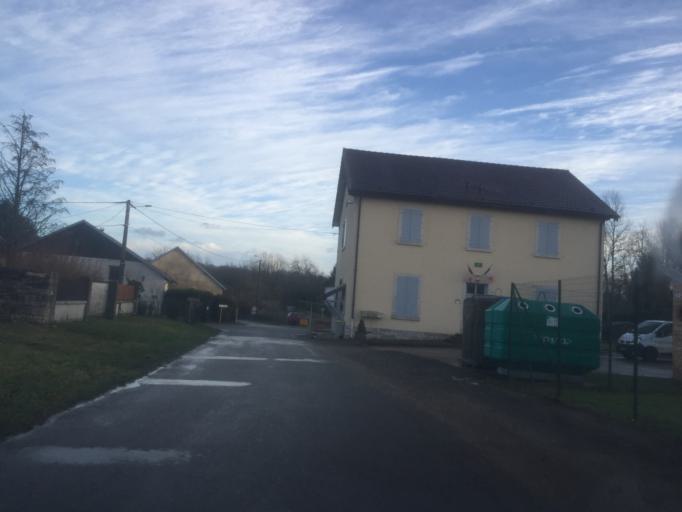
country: FR
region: Franche-Comte
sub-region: Departement du Jura
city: Dampierre
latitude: 47.1245
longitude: 5.7110
